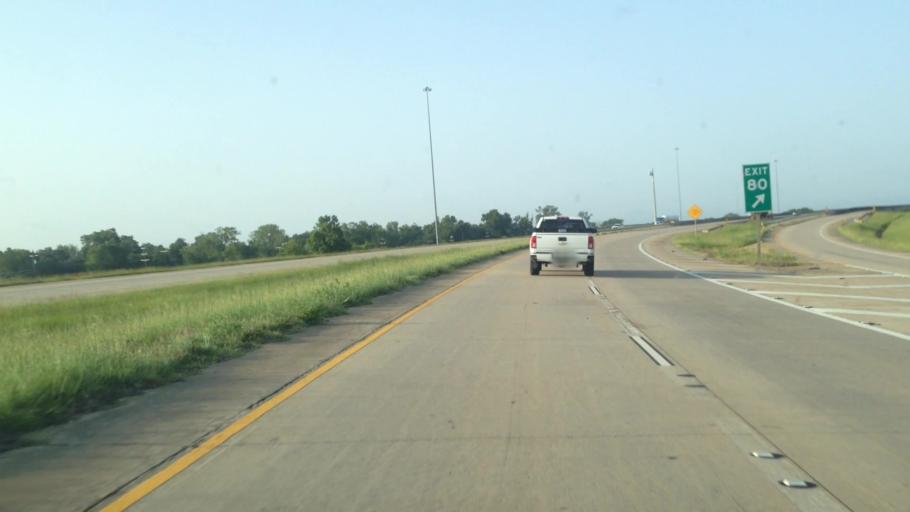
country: US
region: Louisiana
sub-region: Rapides Parish
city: Alexandria
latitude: 31.2468
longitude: -92.4289
